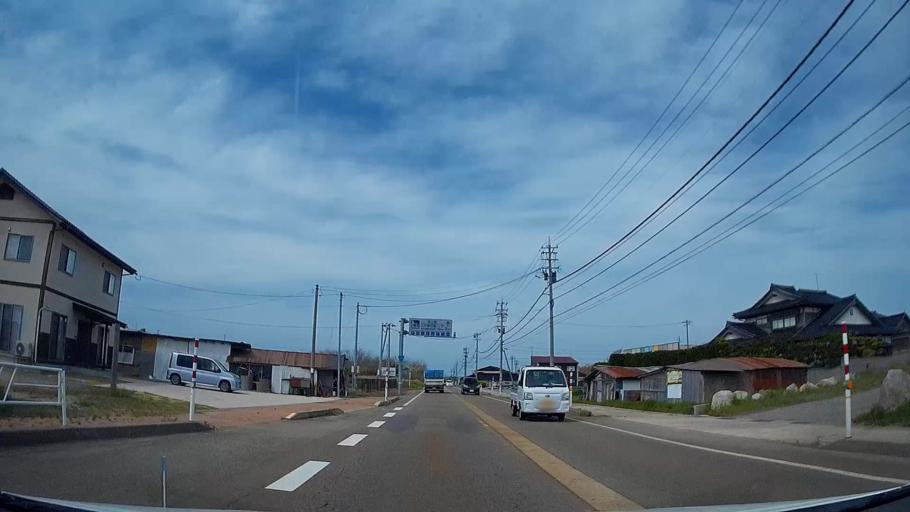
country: JP
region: Ishikawa
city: Hakui
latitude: 36.9889
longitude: 136.7762
